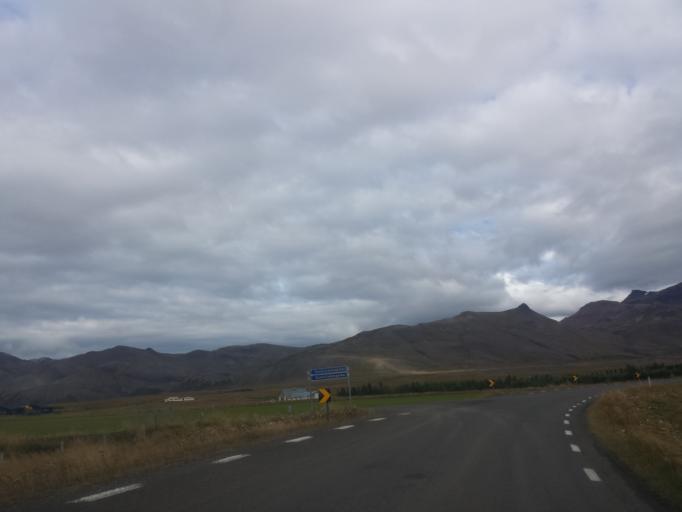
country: IS
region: West
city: Borgarnes
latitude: 64.4111
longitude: -21.8493
